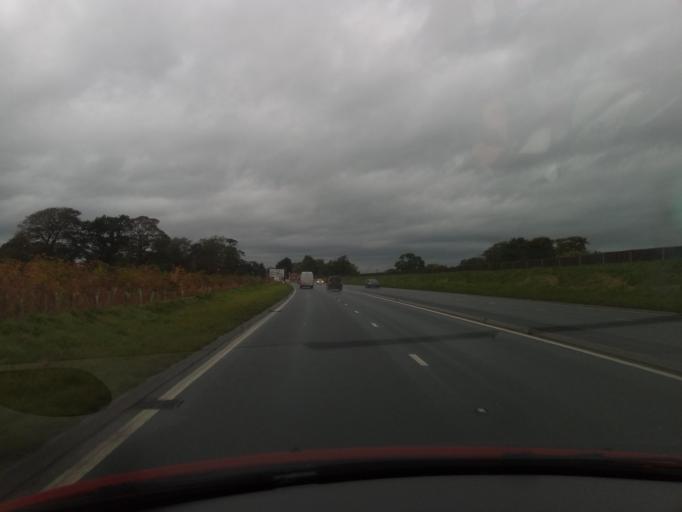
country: GB
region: England
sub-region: Lancashire
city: Preston
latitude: 53.8086
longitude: -2.7150
